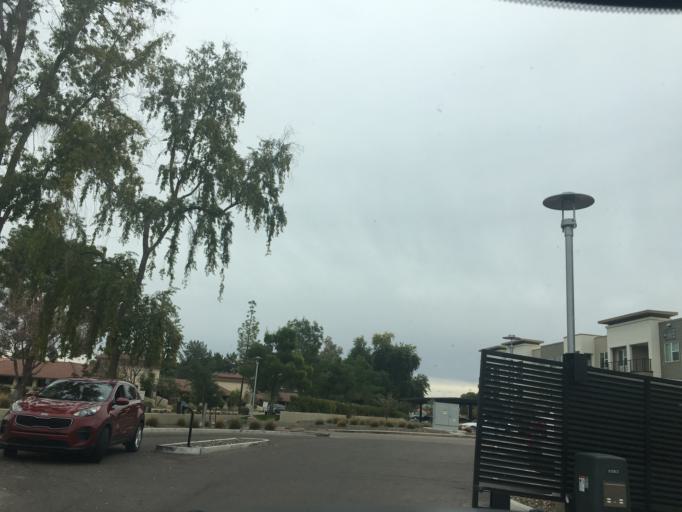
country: US
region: Arizona
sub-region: Maricopa County
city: Tempe
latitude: 33.3807
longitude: -111.9230
